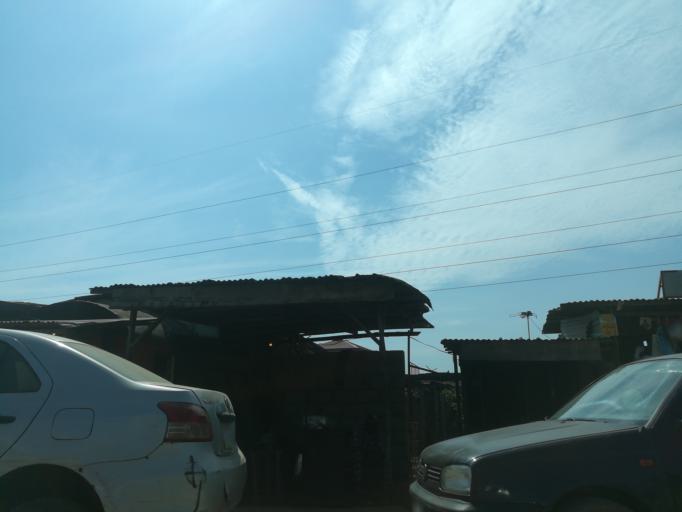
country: NG
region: Lagos
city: Ebute Ikorodu
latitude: 6.6255
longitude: 3.4828
